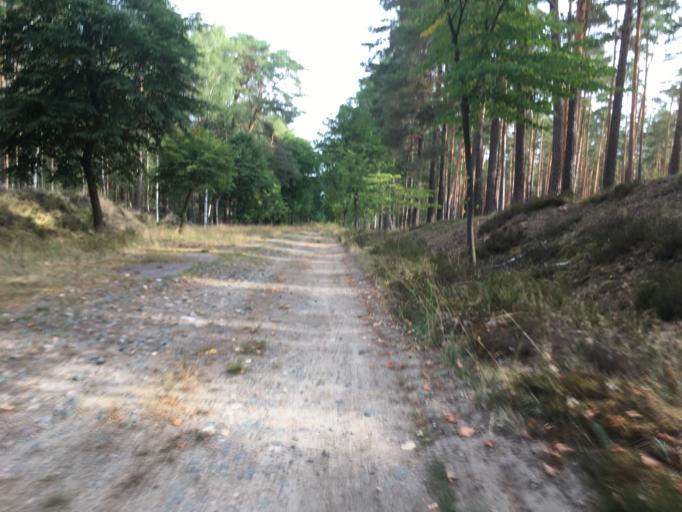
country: DE
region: Brandenburg
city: Marienwerder
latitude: 52.9553
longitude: 13.5253
